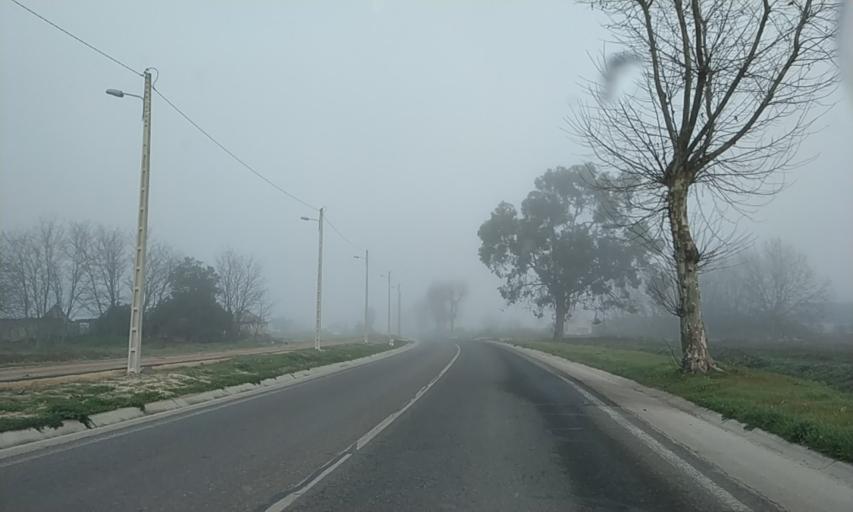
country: PT
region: Setubal
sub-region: Palmela
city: Pinhal Novo
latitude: 38.6549
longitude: -8.9186
